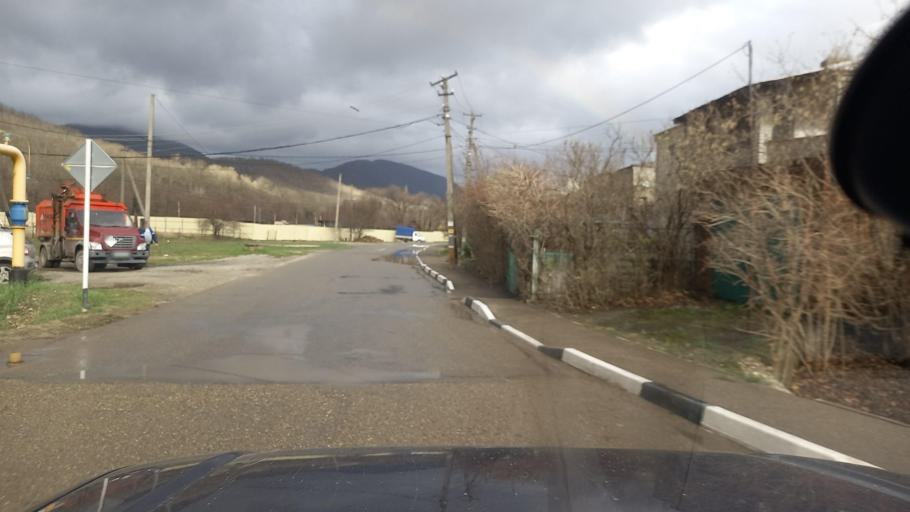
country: RU
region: Krasnodarskiy
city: Pshada
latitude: 44.4767
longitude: 38.3994
